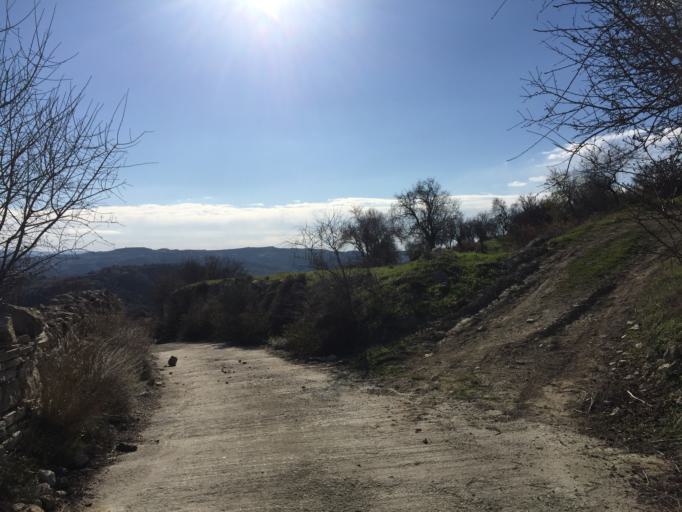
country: CY
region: Pafos
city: Mesogi
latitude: 34.8380
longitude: 32.5105
